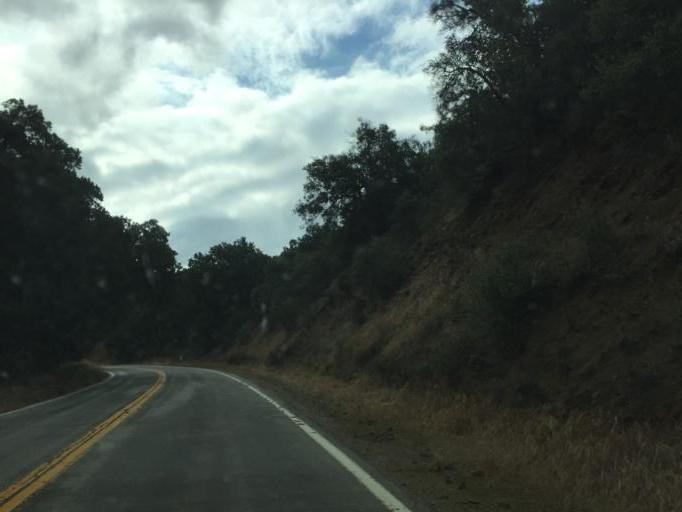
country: US
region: California
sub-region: Los Angeles County
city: Green Valley
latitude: 34.5835
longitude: -118.3551
